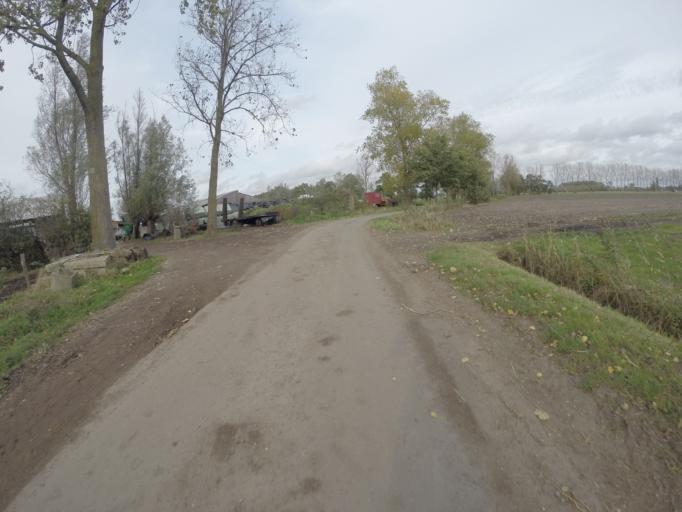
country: BE
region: Flanders
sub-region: Provincie Oost-Vlaanderen
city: Maldegem
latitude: 51.1822
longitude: 3.4289
